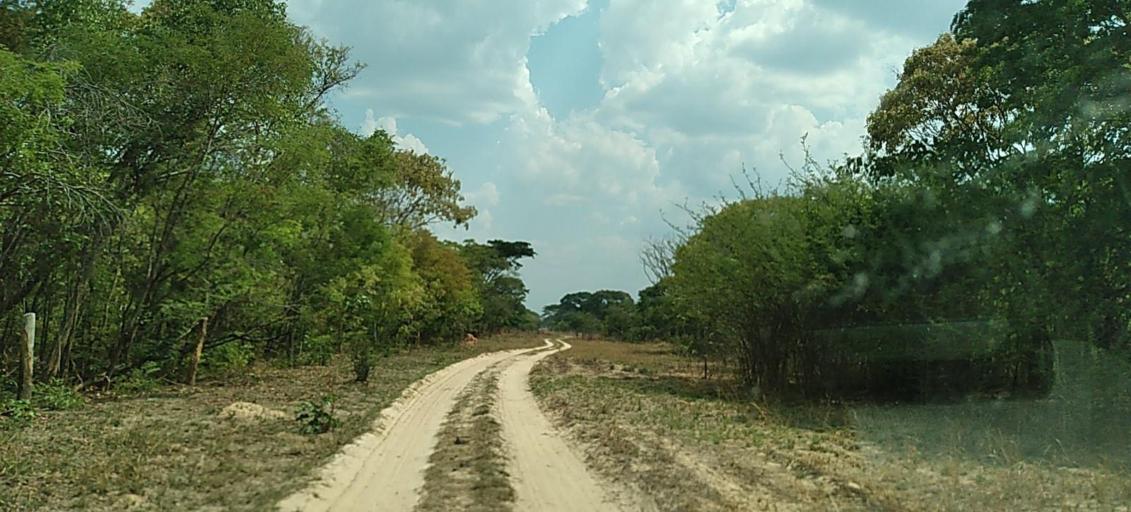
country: ZM
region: Copperbelt
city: Mpongwe
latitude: -13.8314
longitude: 27.9396
